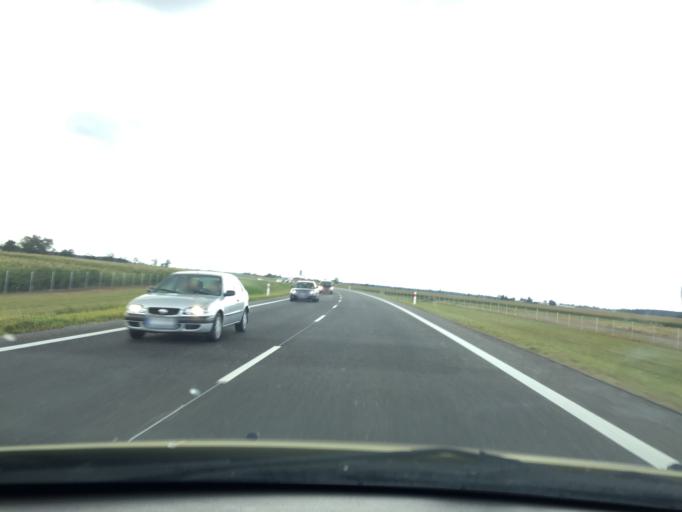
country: PL
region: Greater Poland Voivodeship
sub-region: Powiat sredzki
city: Nowe Miasto nad Warta
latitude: 52.0431
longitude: 17.4590
